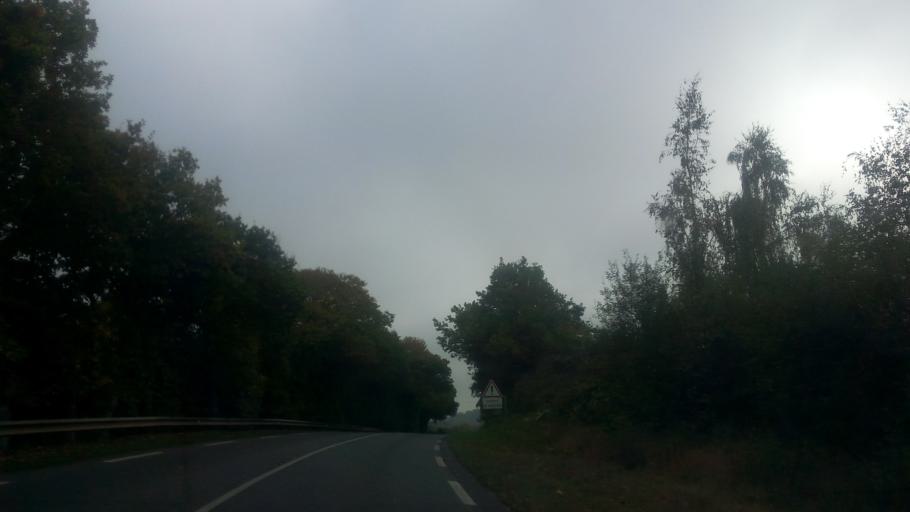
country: FR
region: Pays de la Loire
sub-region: Departement de la Loire-Atlantique
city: Guemene-Penfao
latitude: 47.6366
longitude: -1.9088
